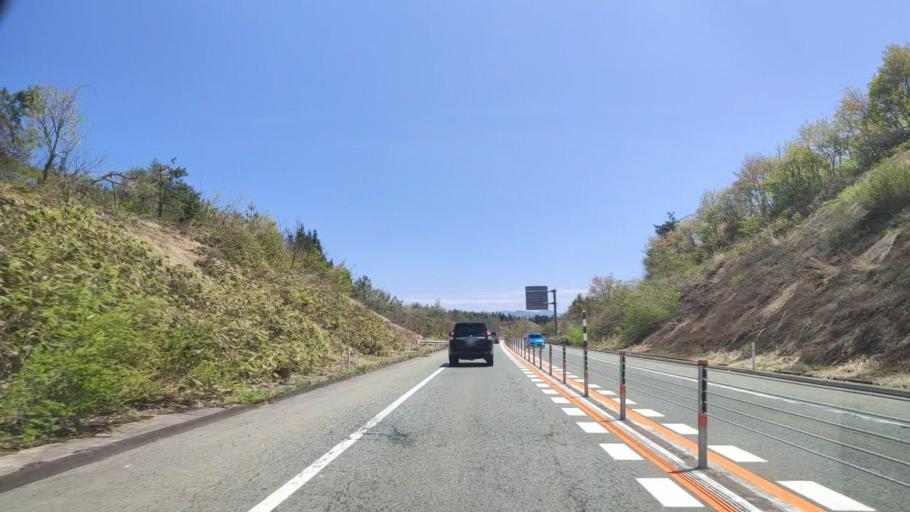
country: JP
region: Yamagata
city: Obanazawa
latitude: 38.6521
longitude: 140.3695
